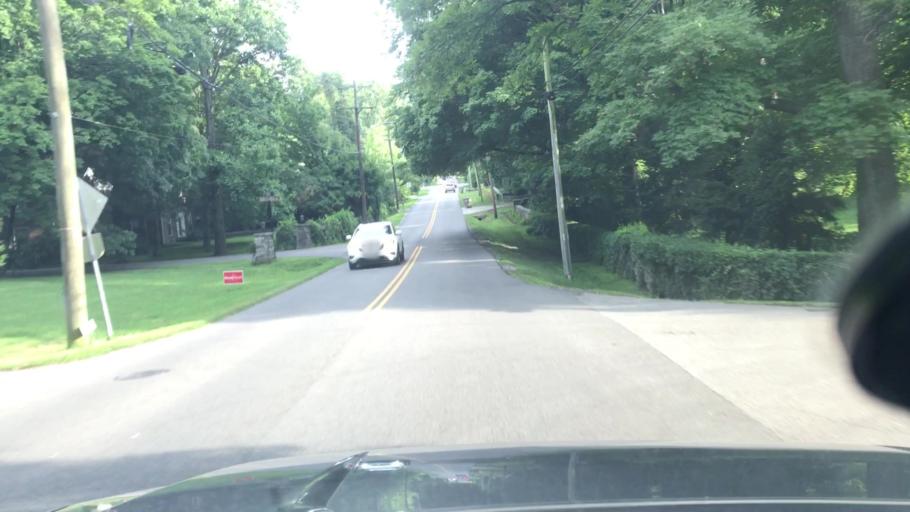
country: US
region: Tennessee
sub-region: Davidson County
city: Belle Meade
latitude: 36.1259
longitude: -86.8264
